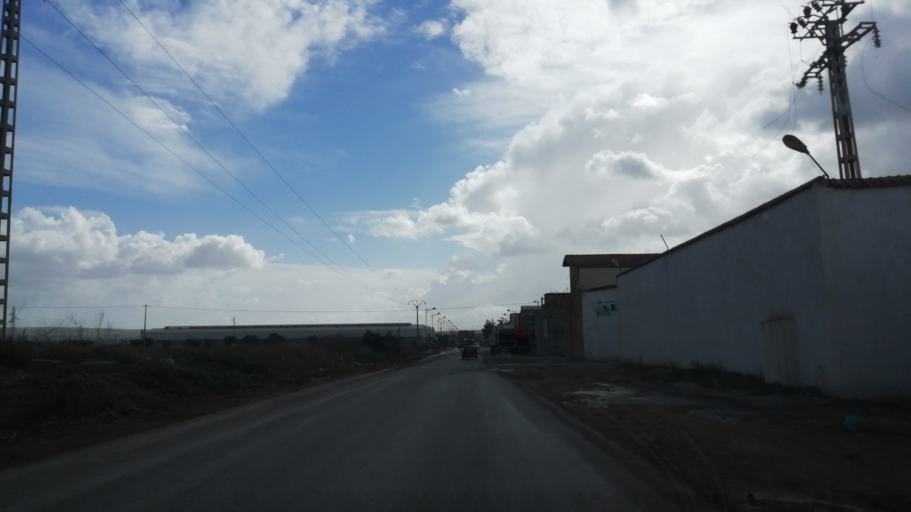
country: DZ
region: Oran
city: Sidi ech Chahmi
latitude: 35.6441
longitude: -0.5568
